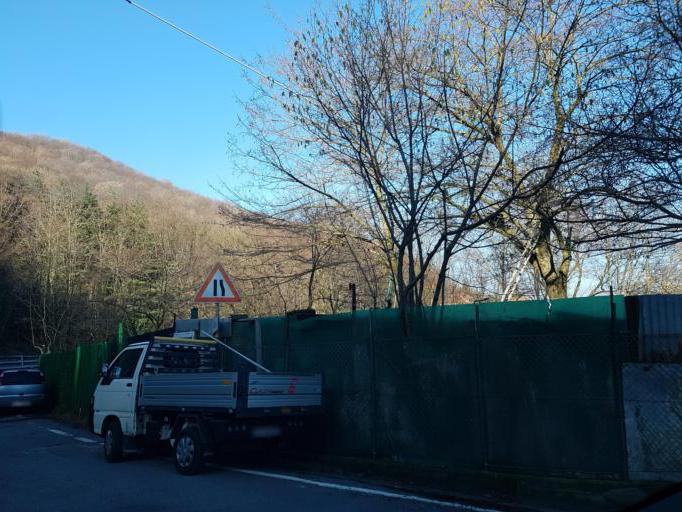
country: IT
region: Liguria
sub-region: Provincia di Genova
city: Manesseno
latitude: 44.4651
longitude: 8.9482
